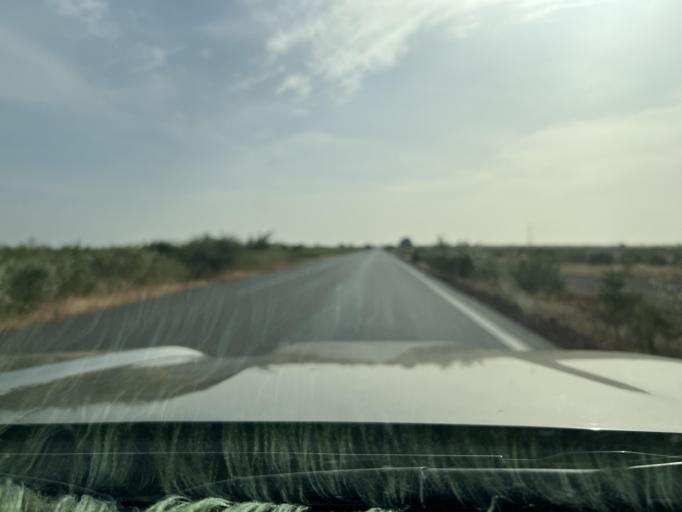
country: ML
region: Segou
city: Baroueli
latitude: 12.9599
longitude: -6.7243
